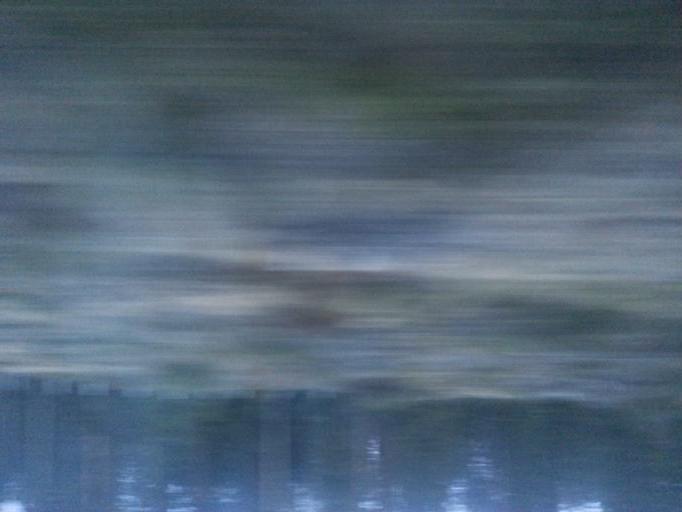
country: NO
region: Sor-Trondelag
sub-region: Rennebu
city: Berkak
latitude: 62.7103
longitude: 9.9629
